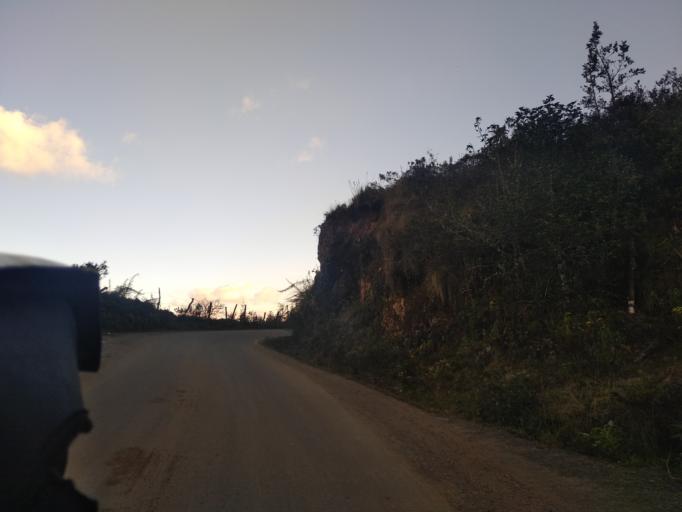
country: PE
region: Amazonas
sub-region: Provincia de Chachapoyas
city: Montevideo
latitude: -6.7183
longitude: -77.8738
